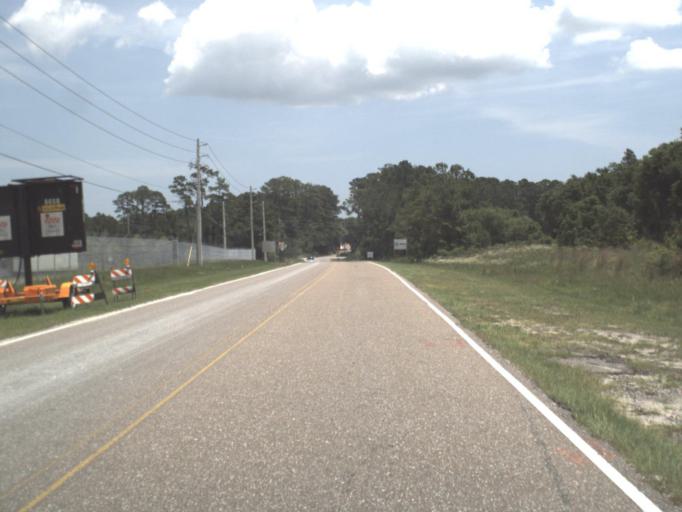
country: US
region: Florida
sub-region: Duval County
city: Jacksonville
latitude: 30.4022
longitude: -81.5636
